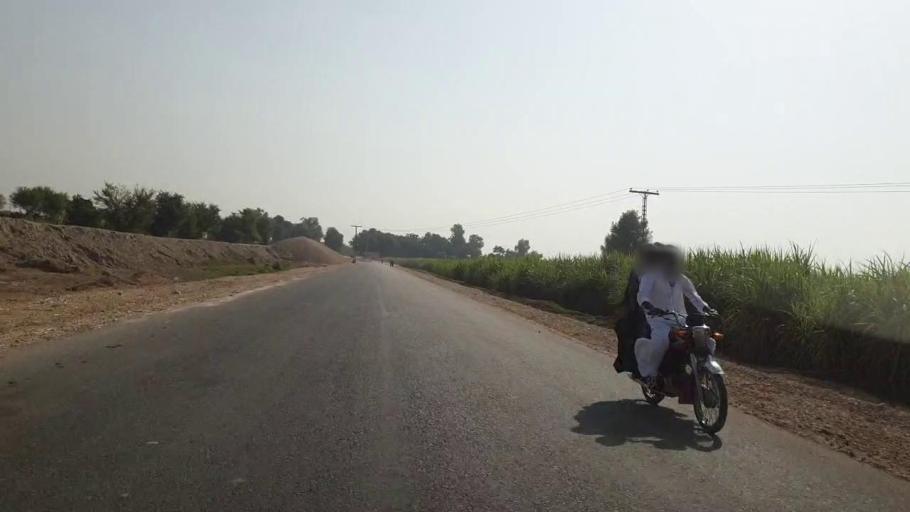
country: PK
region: Sindh
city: Bhan
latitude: 26.6024
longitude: 67.7793
